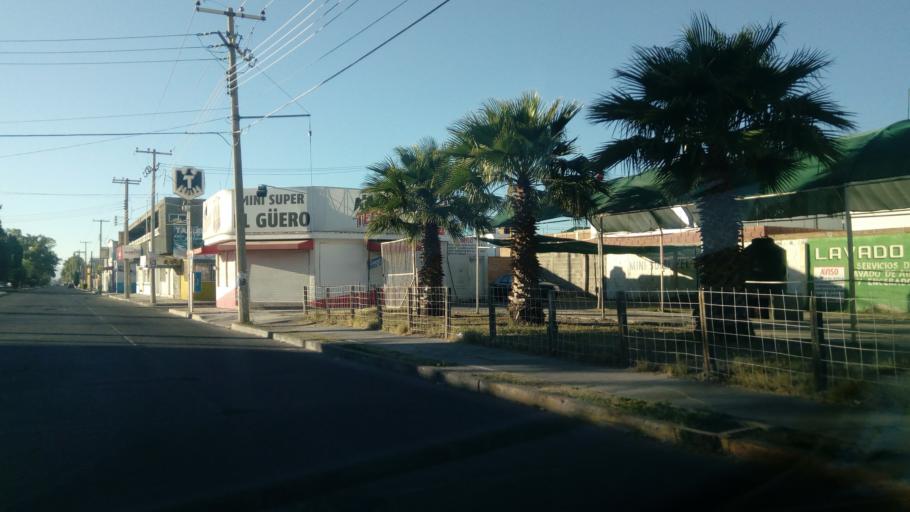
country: MX
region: Durango
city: Victoria de Durango
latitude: 24.0659
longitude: -104.5997
